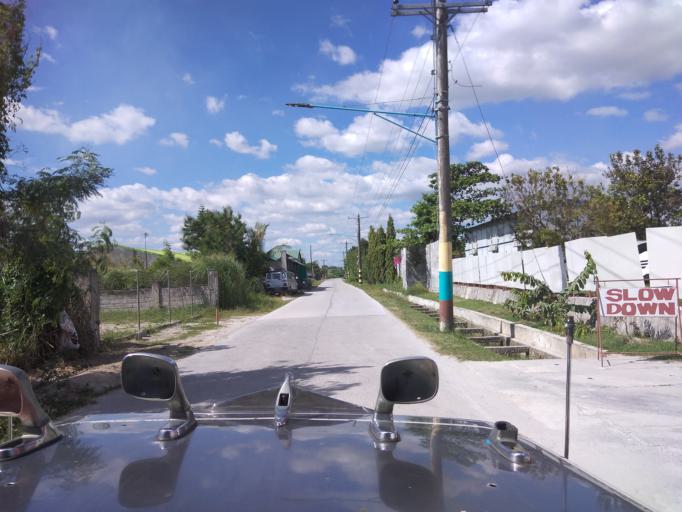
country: PH
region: Central Luzon
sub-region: Province of Pampanga
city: Bacolor
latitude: 15.0228
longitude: 120.6381
